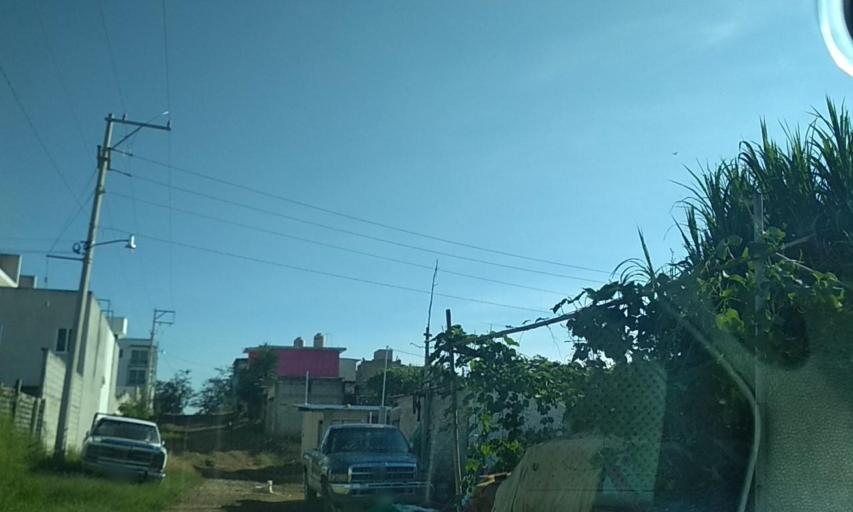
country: MX
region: Veracruz
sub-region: Xalapa
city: Colonia Santa Barbara
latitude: 19.4959
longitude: -96.8748
